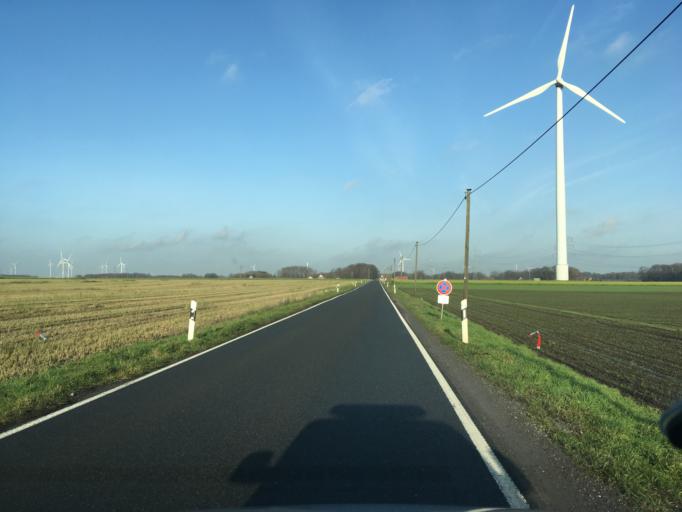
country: DE
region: North Rhine-Westphalia
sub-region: Regierungsbezirk Munster
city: Velen
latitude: 51.9232
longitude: 6.9637
